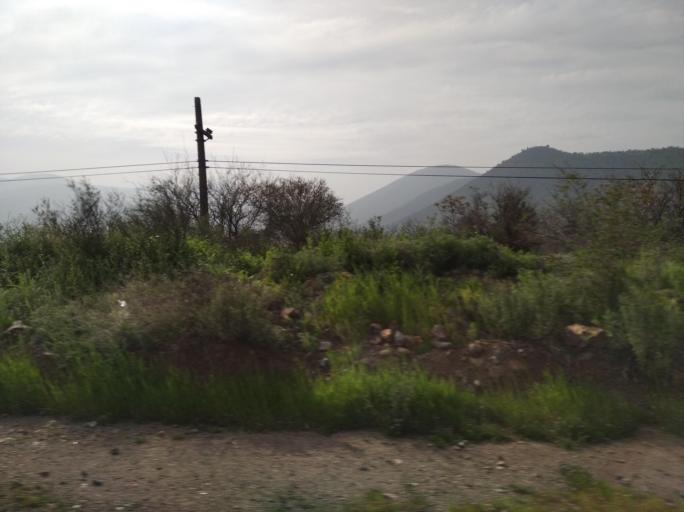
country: CL
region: Santiago Metropolitan
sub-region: Provincia de Chacabuco
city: Lampa
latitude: -33.1342
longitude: -70.9195
